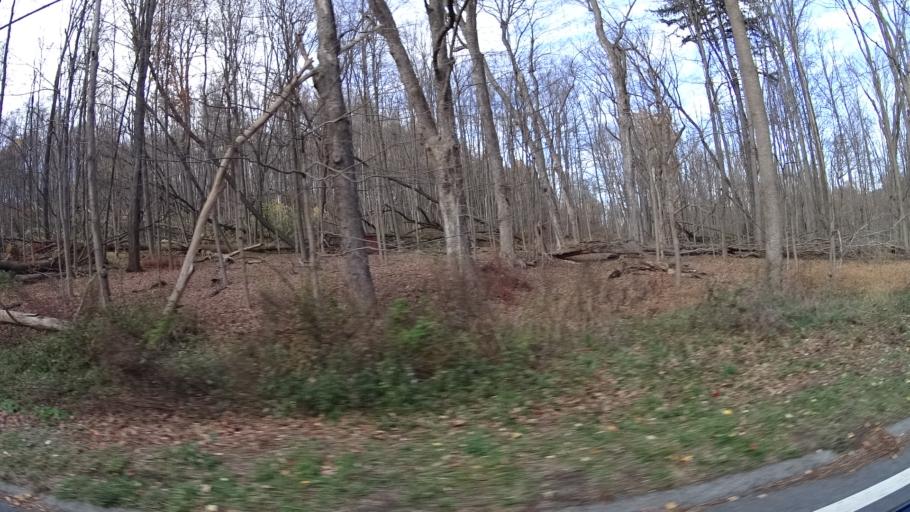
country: US
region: New Jersey
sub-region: Morris County
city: Morristown
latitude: 40.7919
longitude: -74.5209
